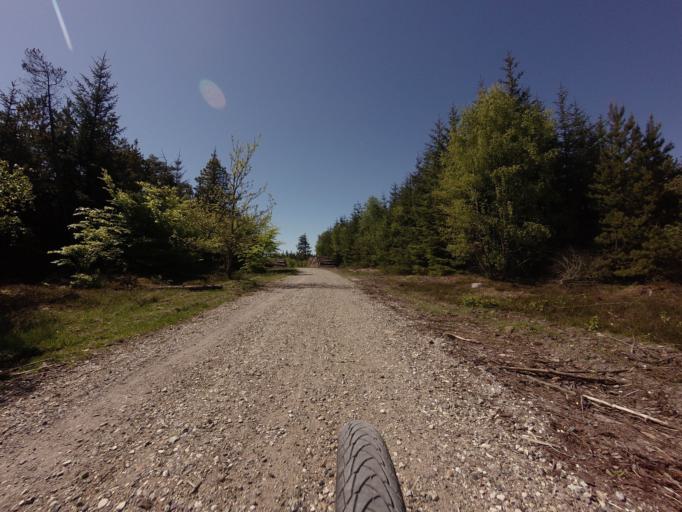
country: DK
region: North Denmark
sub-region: Jammerbugt Kommune
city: Pandrup
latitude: 57.2408
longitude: 9.5852
